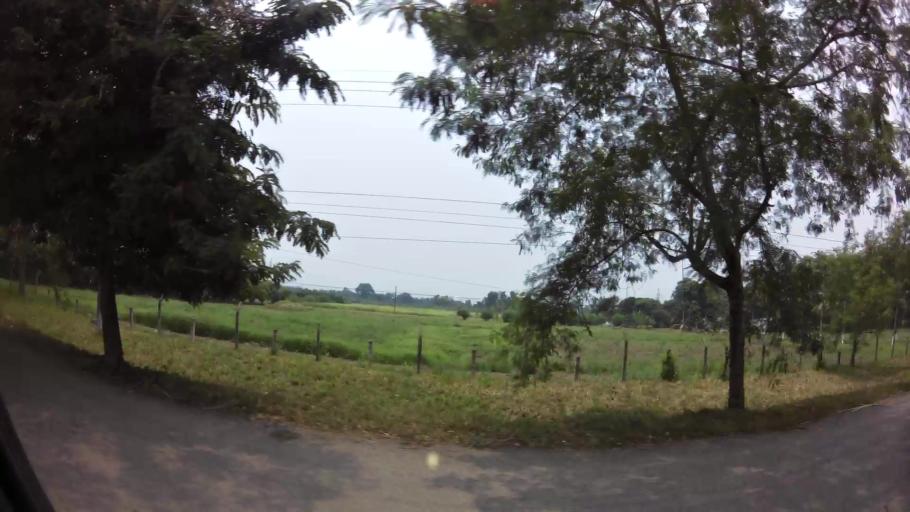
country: HN
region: Yoro
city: El Progreso
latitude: 15.4067
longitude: -87.8292
